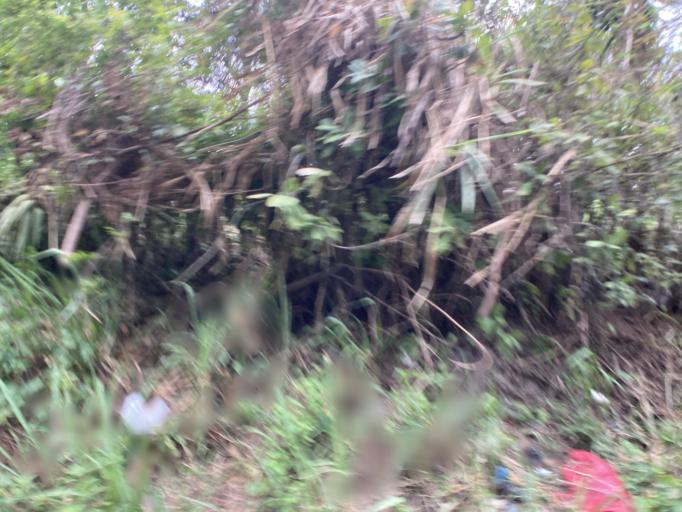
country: GT
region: Guatemala
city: Fraijanes
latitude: 14.3946
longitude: -90.4713
